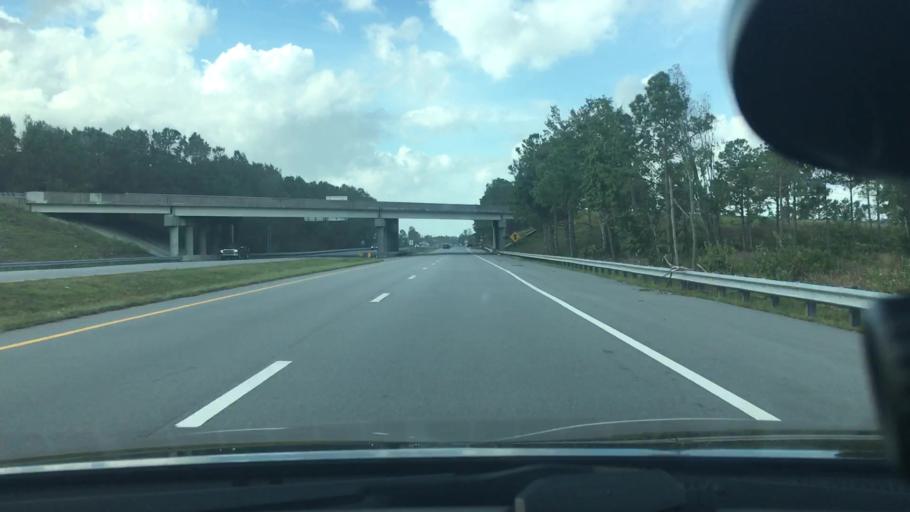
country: US
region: North Carolina
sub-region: Craven County
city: New Bern
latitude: 35.1142
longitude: -77.0116
